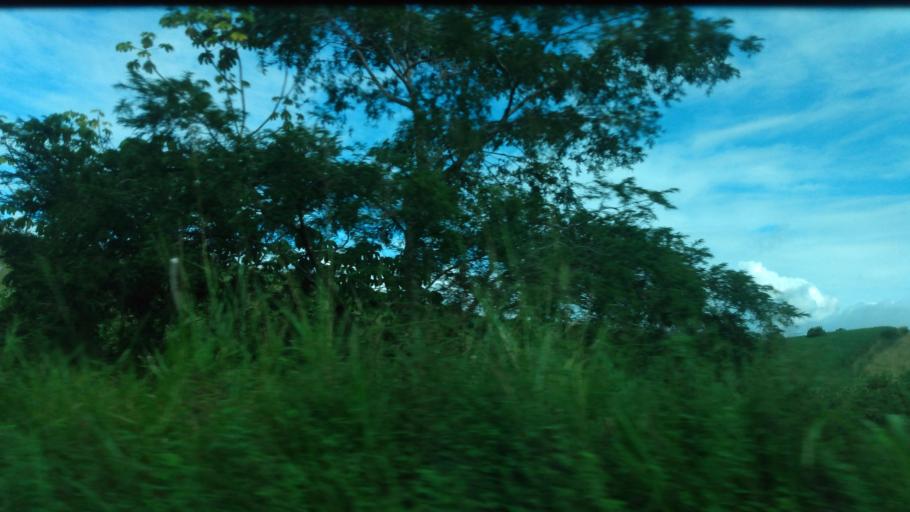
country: BR
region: Pernambuco
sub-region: Catende
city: Catende
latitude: -8.6894
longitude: -35.7073
